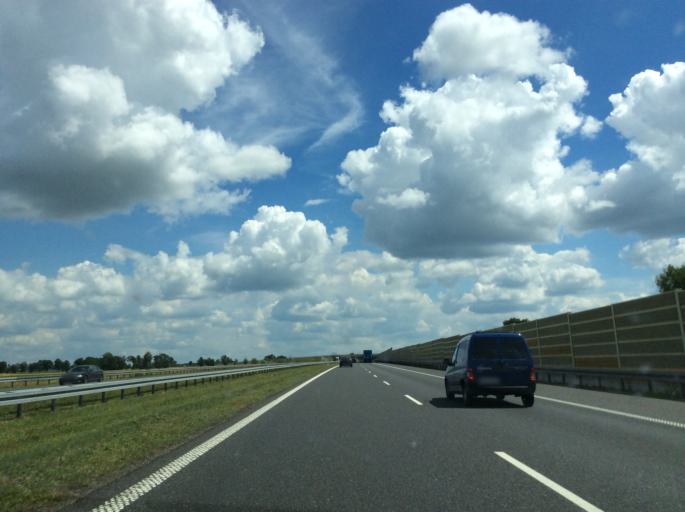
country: PL
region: Lodz Voivodeship
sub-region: Powiat poddebicki
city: Dalikow
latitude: 51.9636
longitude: 19.1158
